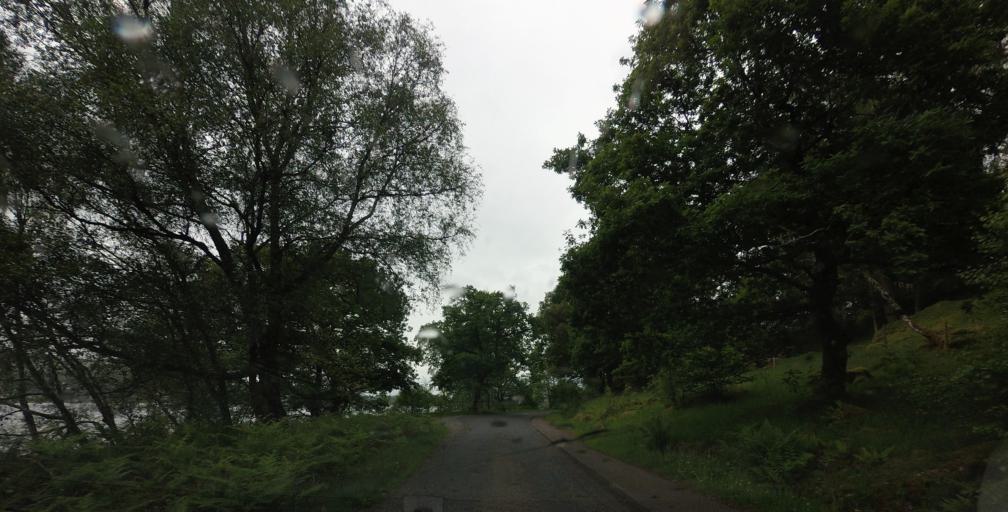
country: GB
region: Scotland
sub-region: Highland
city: Fort William
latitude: 56.8362
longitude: -5.1403
